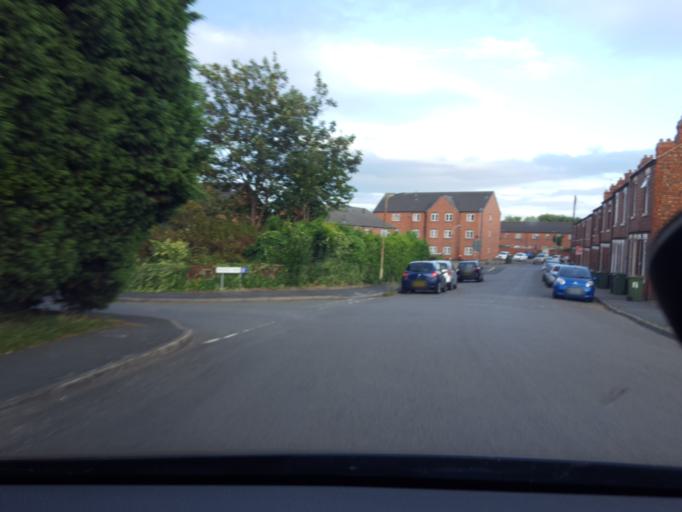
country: GB
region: England
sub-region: Leicestershire
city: Loughborough
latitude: 52.7724
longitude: -1.1942
